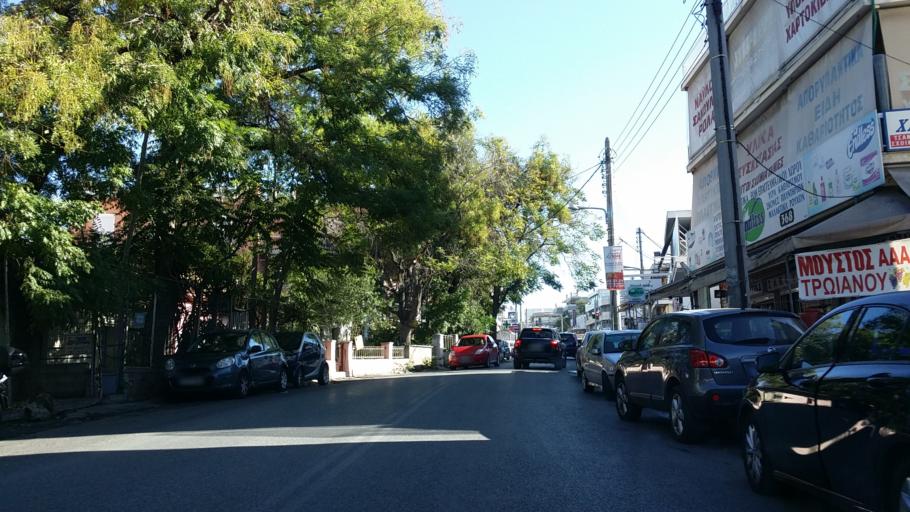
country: GR
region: Attica
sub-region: Nomarchia Athinas
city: Irakleio
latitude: 38.0492
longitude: 23.7626
